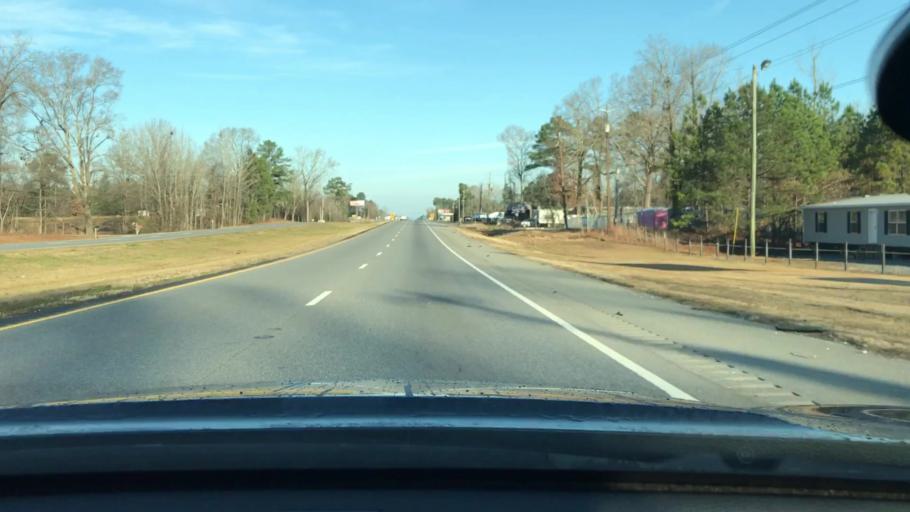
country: US
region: Alabama
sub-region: Talladega County
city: Mignon
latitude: 33.2171
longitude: -86.3166
